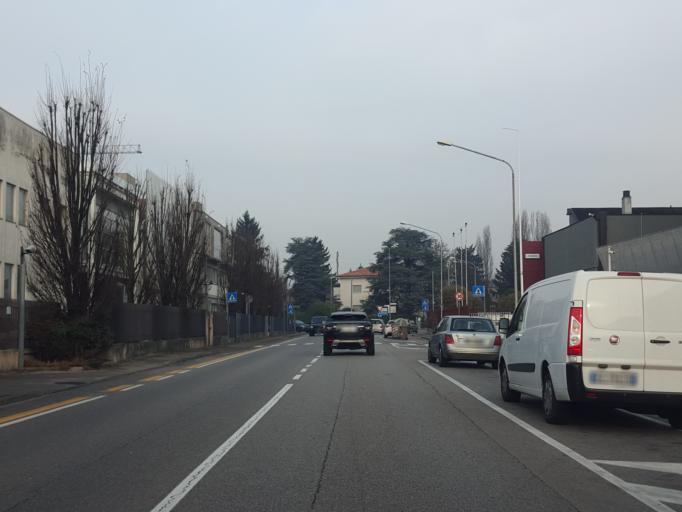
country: IT
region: Veneto
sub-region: Provincia di Vicenza
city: Vicenza
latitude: 45.5467
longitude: 11.5179
